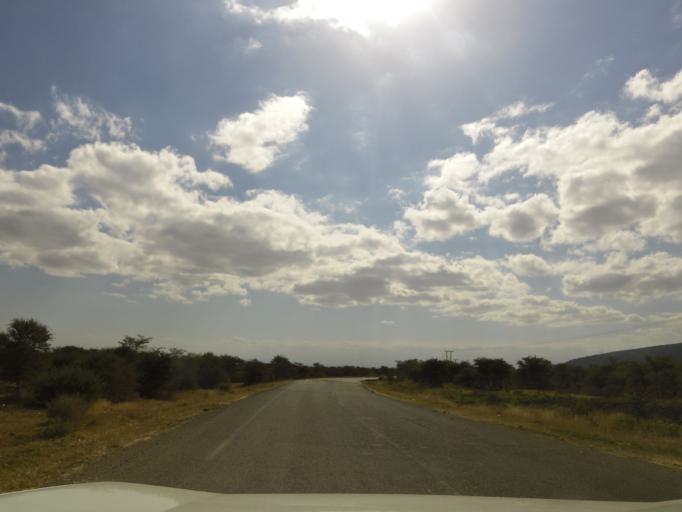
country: TZ
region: Arusha
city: Mto wa Mbu
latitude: -3.5079
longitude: 36.0145
